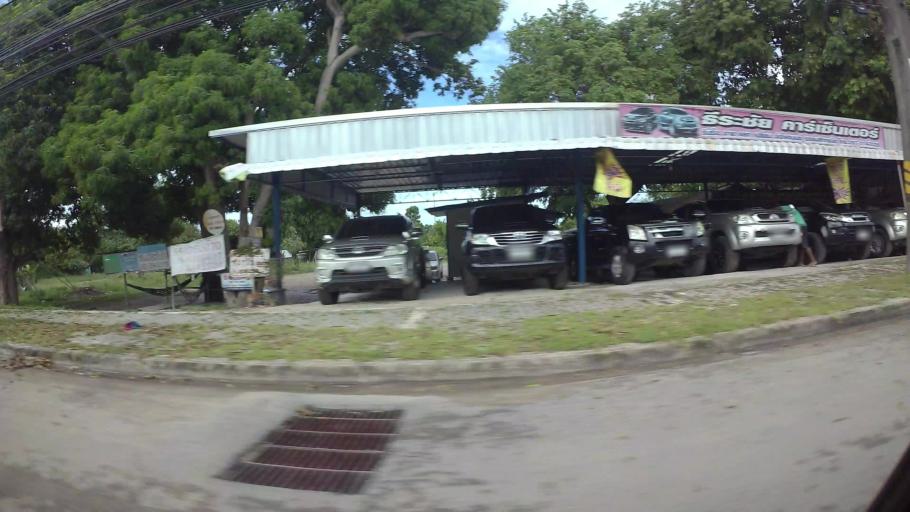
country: TH
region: Rayong
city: Rayong
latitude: 12.7051
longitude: 101.1821
